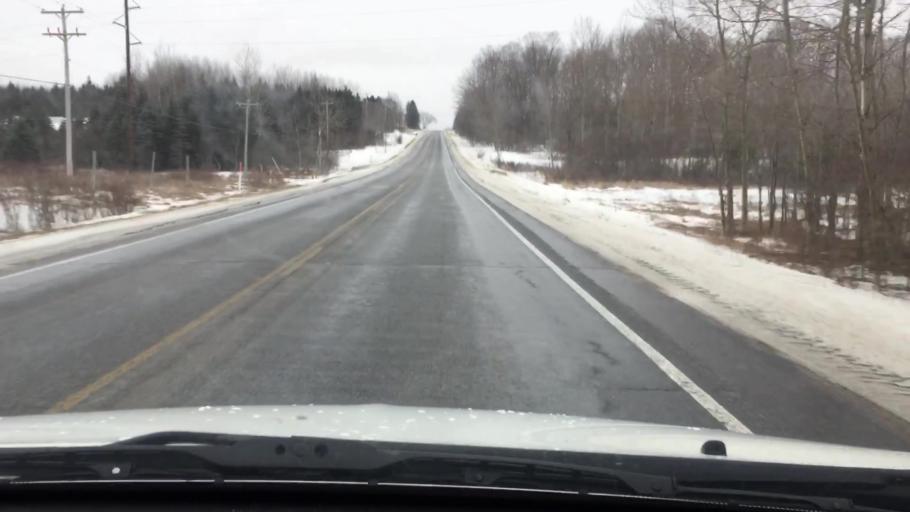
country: US
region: Michigan
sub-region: Osceola County
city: Reed City
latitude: 44.0506
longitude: -85.4439
